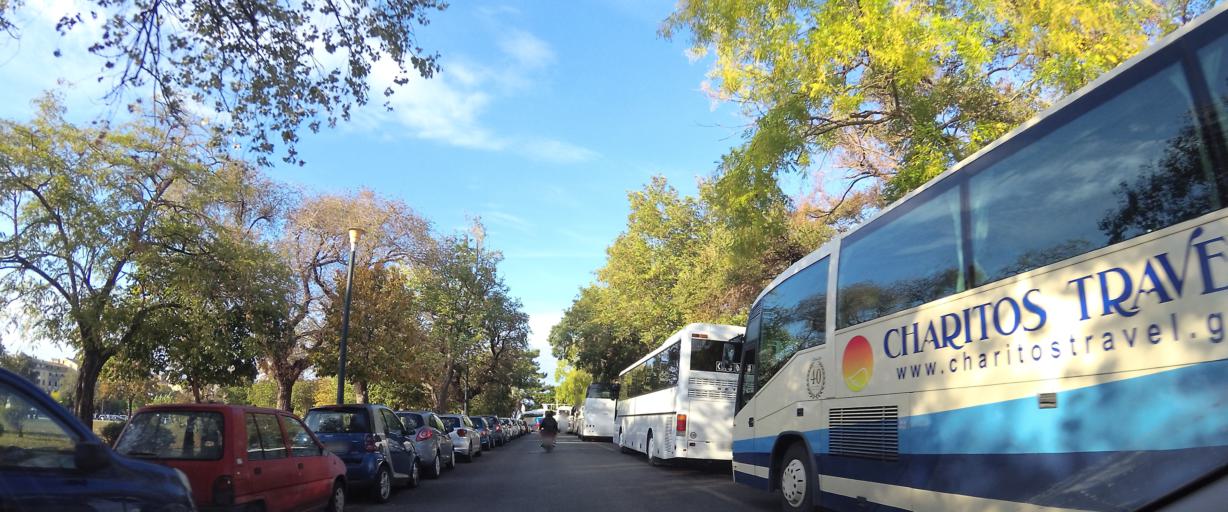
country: GR
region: Ionian Islands
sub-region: Nomos Kerkyras
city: Kerkyra
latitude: 39.6224
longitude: 19.9253
